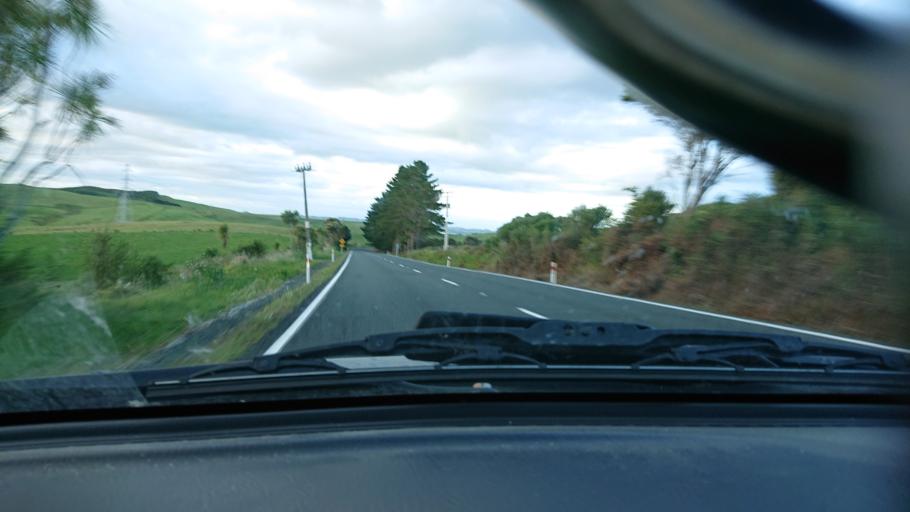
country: NZ
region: Auckland
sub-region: Auckland
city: Parakai
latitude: -36.4710
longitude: 174.4493
